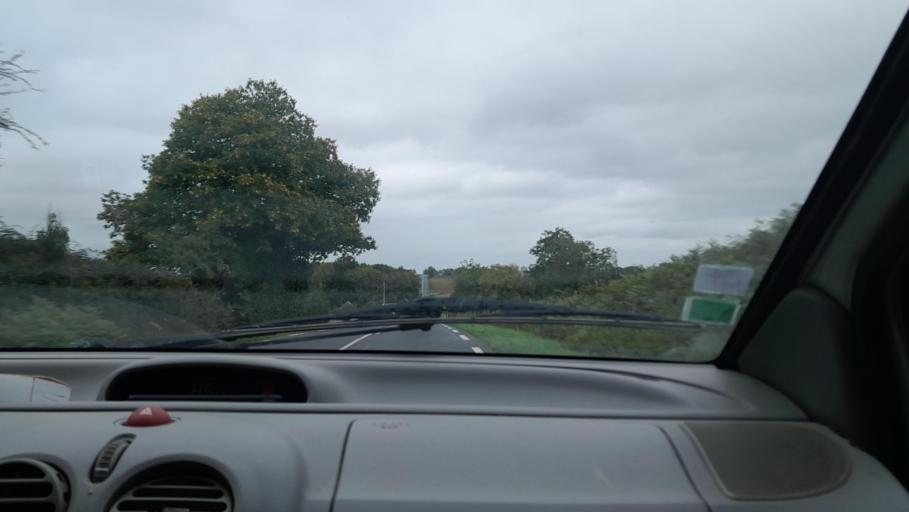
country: FR
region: Pays de la Loire
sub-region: Departement de la Loire-Atlantique
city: Saint-Mars-la-Jaille
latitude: 47.5449
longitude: -1.1861
